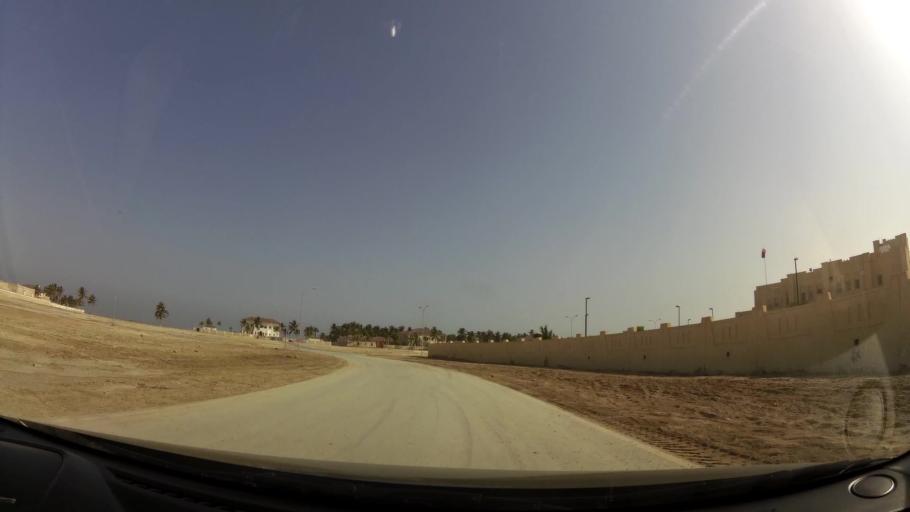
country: OM
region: Zufar
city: Salalah
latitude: 16.9953
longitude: 54.0495
